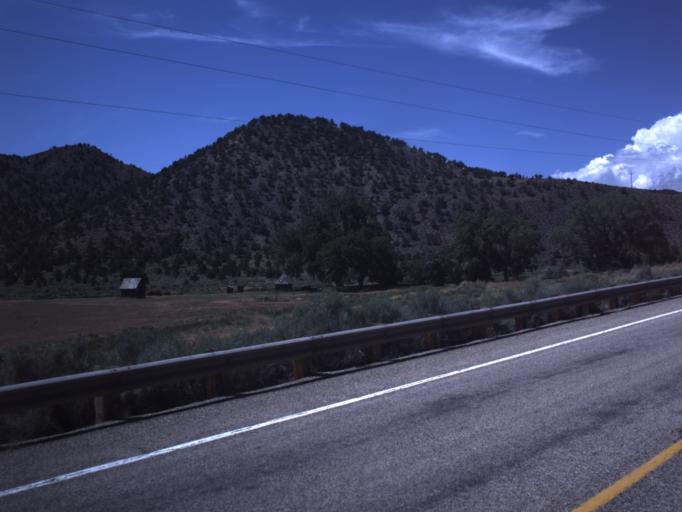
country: US
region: Utah
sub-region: Piute County
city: Junction
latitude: 38.1412
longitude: -112.3090
